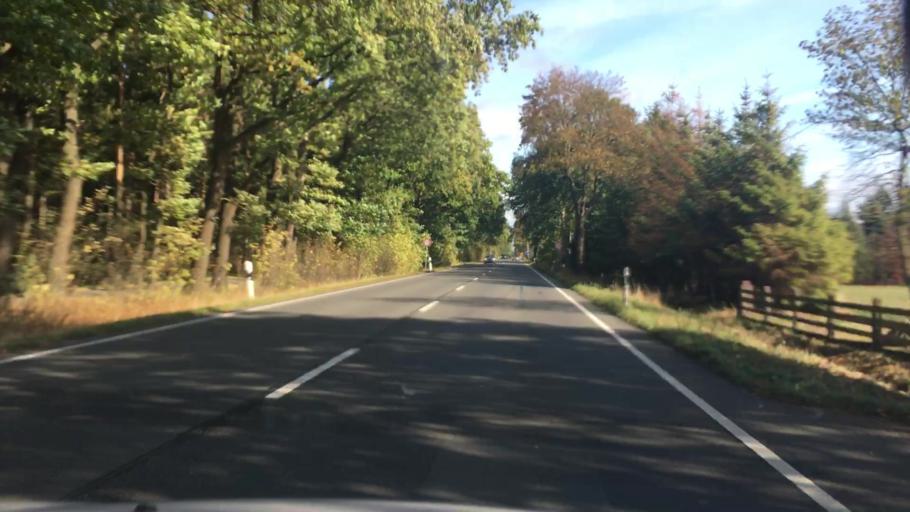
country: DE
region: Lower Saxony
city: Pennigsehl
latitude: 52.6642
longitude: 9.0261
